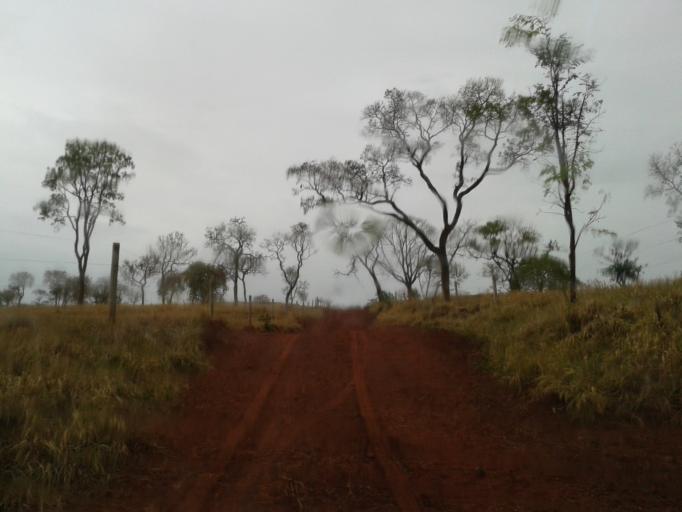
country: BR
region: Minas Gerais
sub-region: Campina Verde
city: Campina Verde
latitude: -19.3462
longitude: -49.5493
